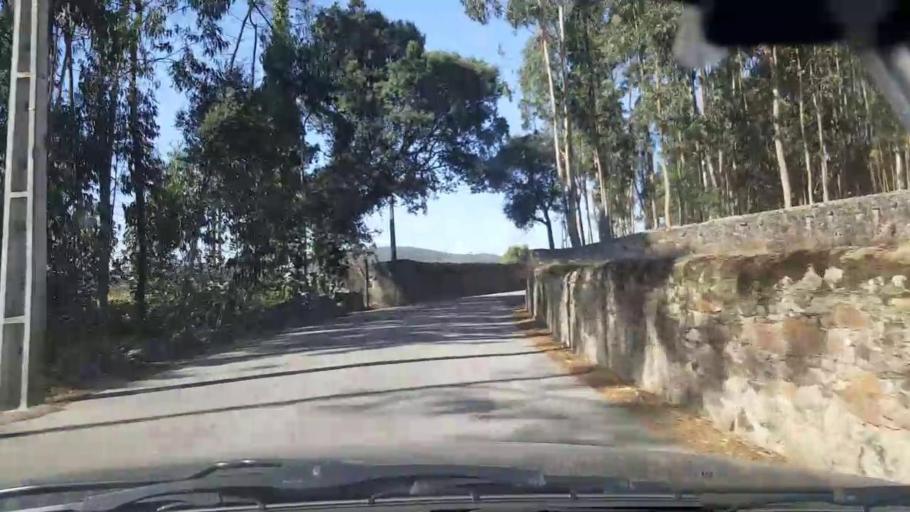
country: PT
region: Porto
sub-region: Vila do Conde
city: Arvore
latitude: 41.3660
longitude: -8.6468
